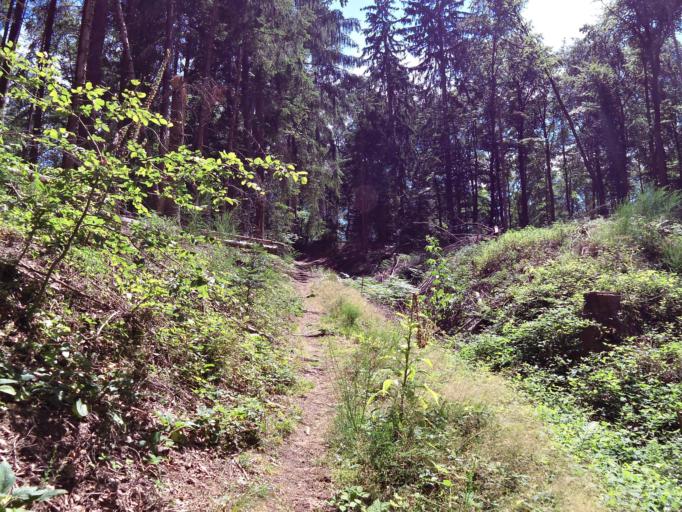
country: DE
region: Rheinland-Pfalz
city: Altleiningen
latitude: 49.4710
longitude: 8.0635
